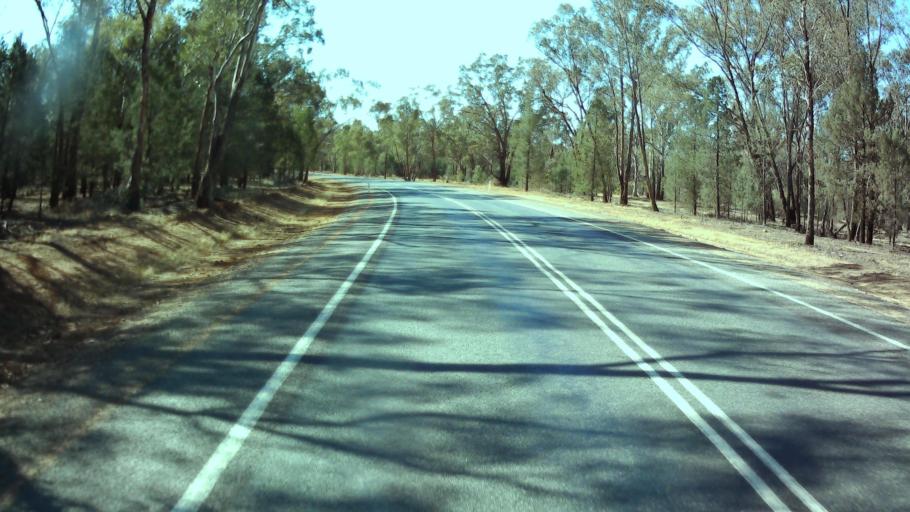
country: AU
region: New South Wales
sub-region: Weddin
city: Grenfell
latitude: -33.7283
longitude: 148.0882
